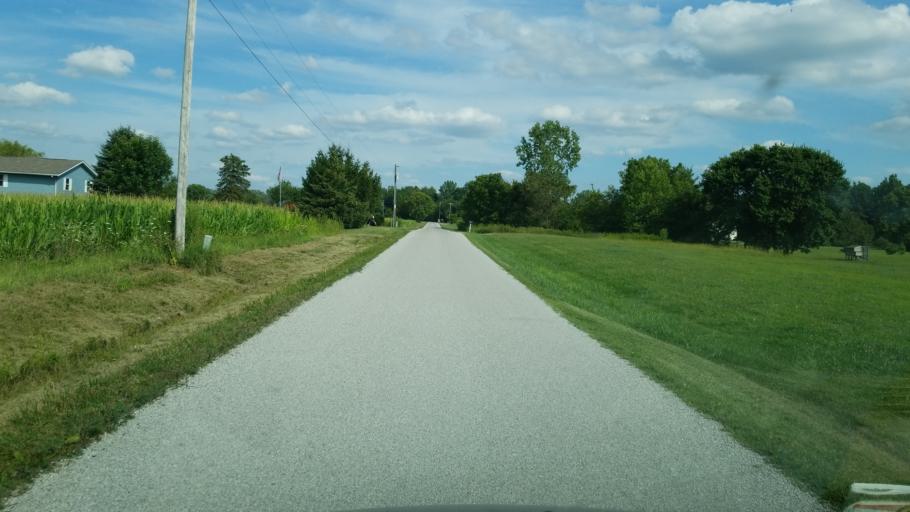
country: US
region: Ohio
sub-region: Delaware County
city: Ashley
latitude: 40.4344
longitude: -83.0036
